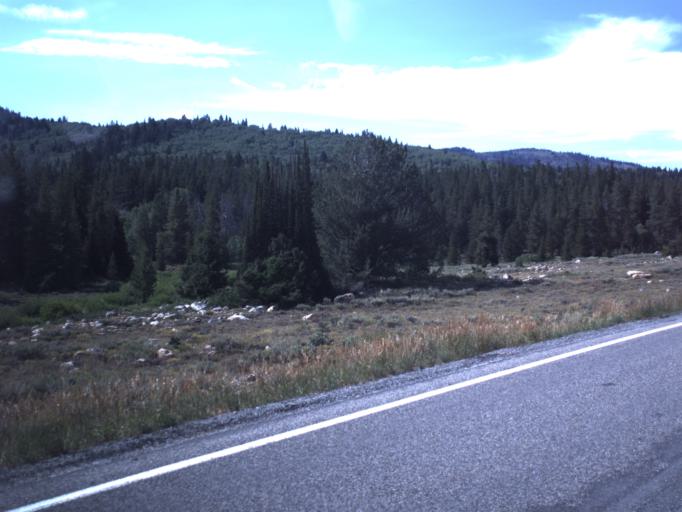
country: US
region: Utah
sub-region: Cache County
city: Richmond
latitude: 41.9662
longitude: -111.5319
